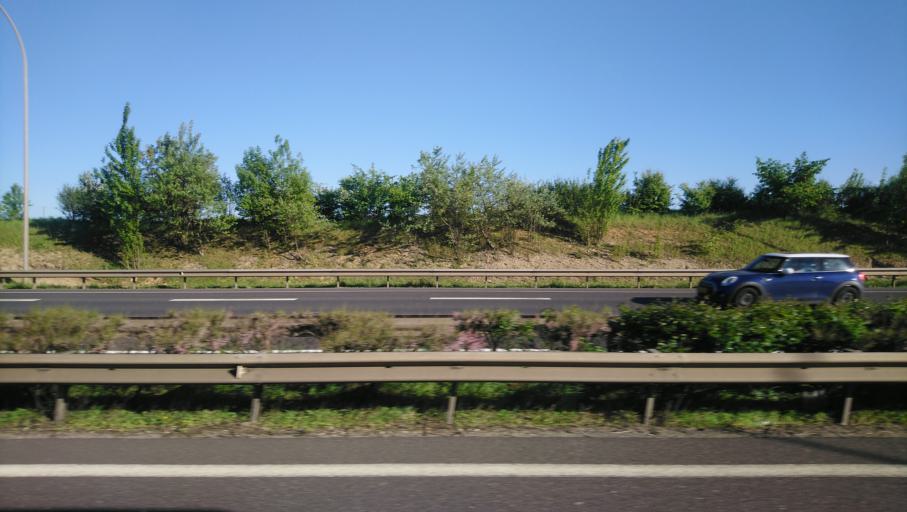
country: LU
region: Luxembourg
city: Pontpierre
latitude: 49.5438
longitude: 6.0374
